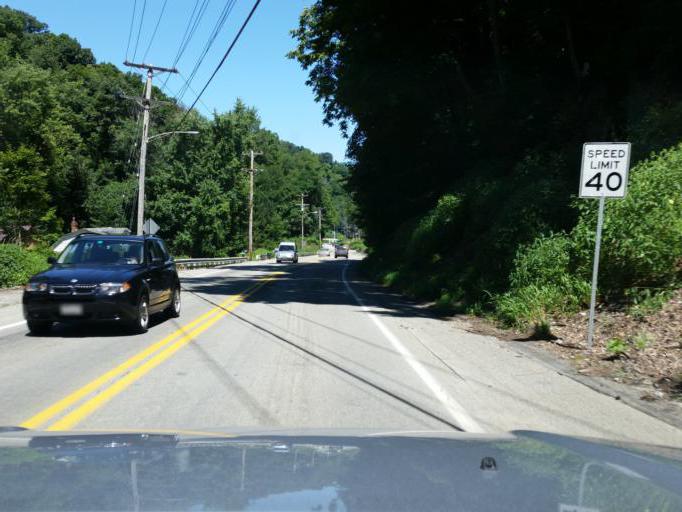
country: US
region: Pennsylvania
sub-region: Allegheny County
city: Blawnox
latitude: 40.4705
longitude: -79.8474
